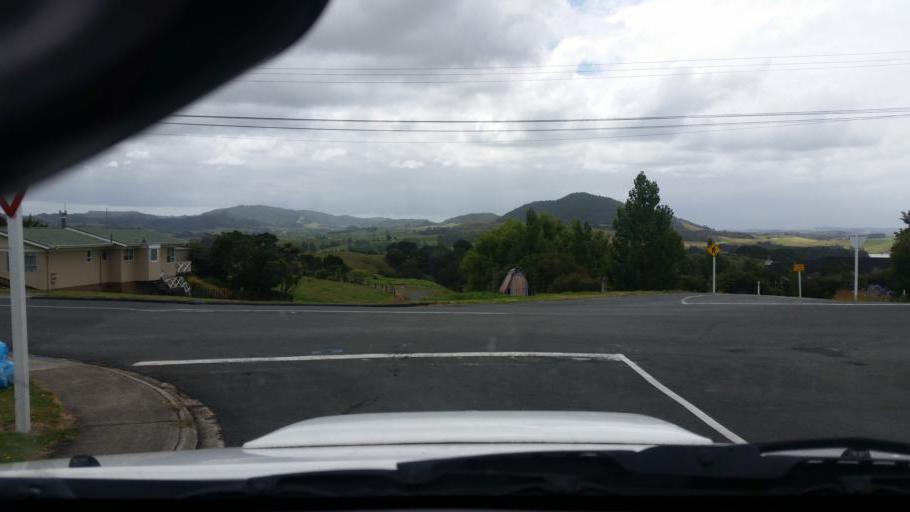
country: NZ
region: Northland
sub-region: Whangarei
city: Ruakaka
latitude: -36.1156
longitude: 174.3496
